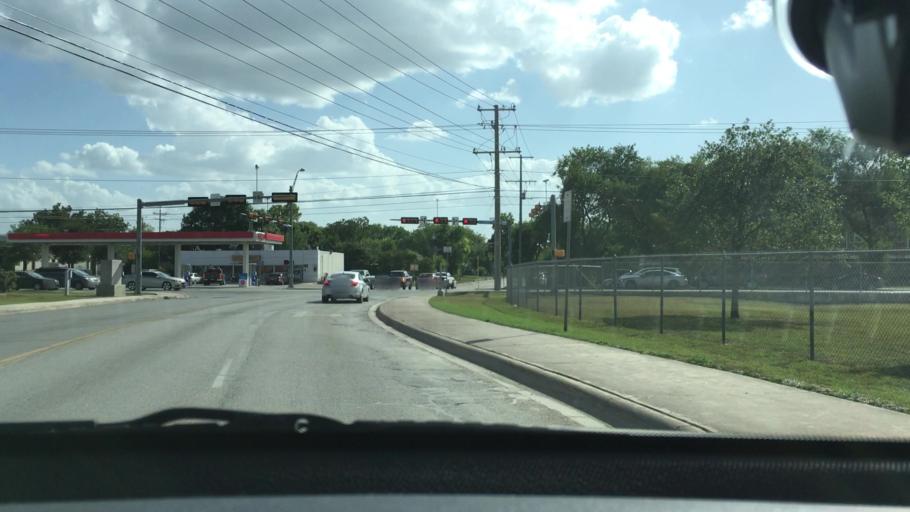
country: US
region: Texas
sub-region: Guadalupe County
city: Schertz
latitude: 29.5614
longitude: -98.2670
